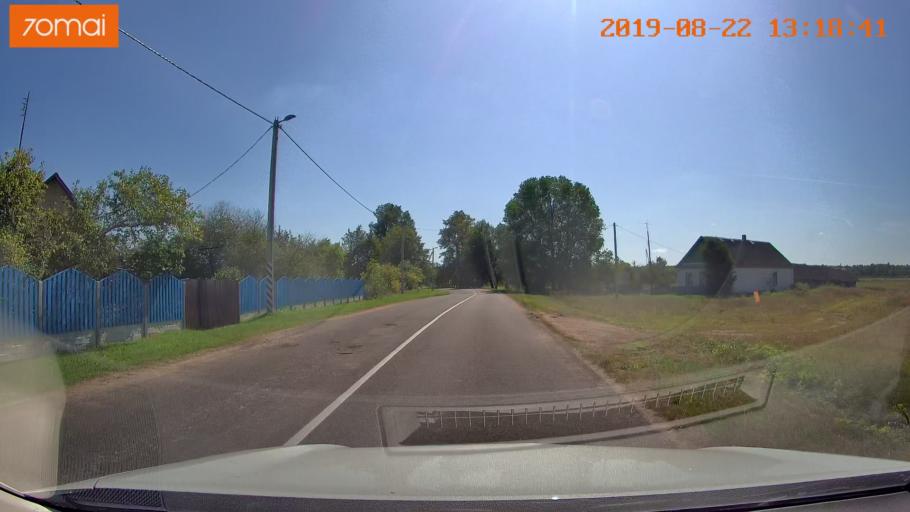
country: BY
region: Minsk
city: Urechcha
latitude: 53.2391
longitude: 27.9422
